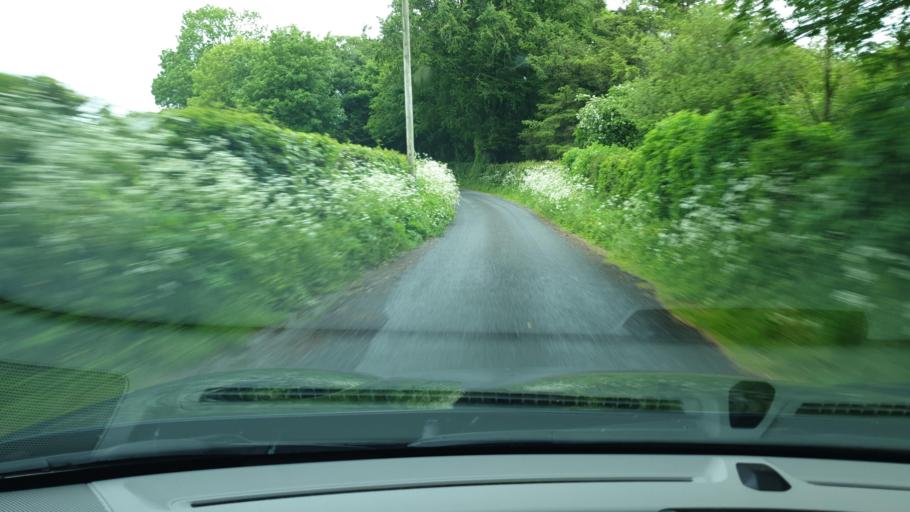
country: IE
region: Leinster
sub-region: Laois
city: Portlaoise
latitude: 53.0359
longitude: -7.3373
